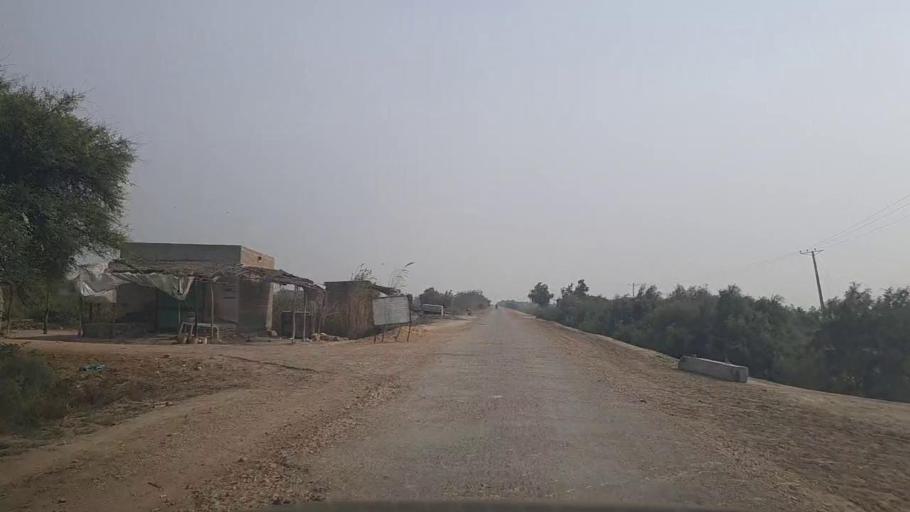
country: PK
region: Sindh
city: Mirpur Sakro
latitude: 24.4727
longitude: 67.6708
